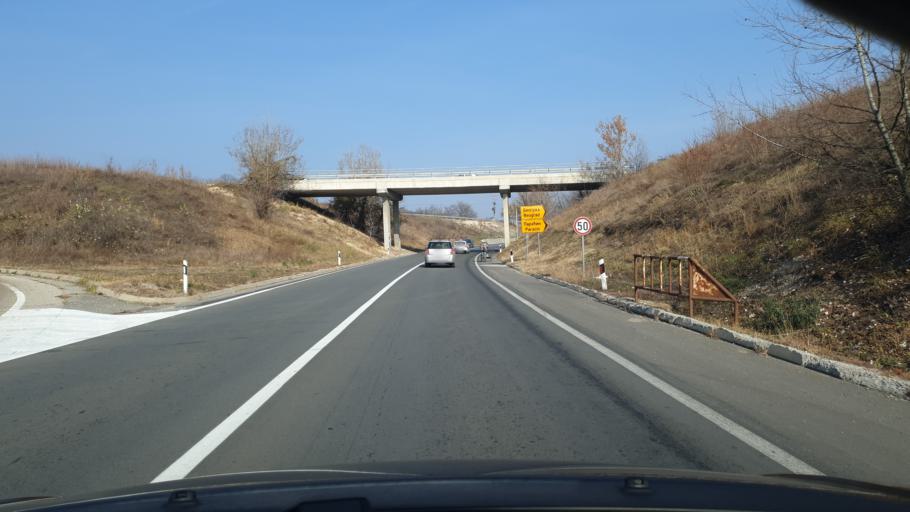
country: RS
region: Central Serbia
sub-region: Zajecarski Okrug
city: Zajecar
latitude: 43.9219
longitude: 22.2948
